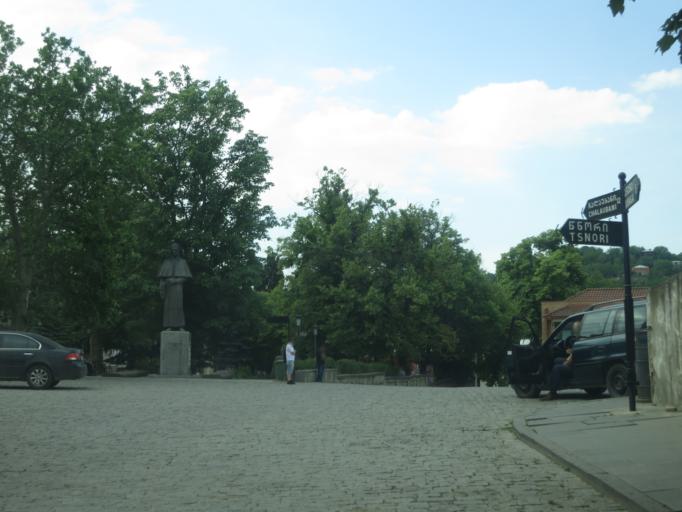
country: GE
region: Kakheti
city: Sighnaghi
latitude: 41.6204
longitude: 45.9225
